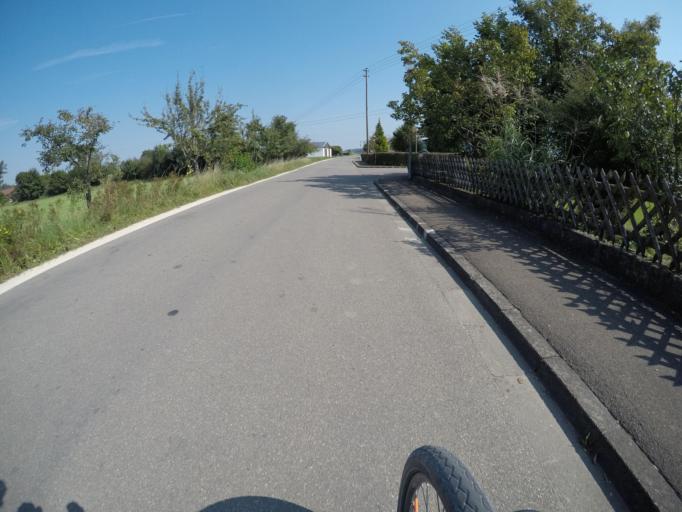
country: DE
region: Bavaria
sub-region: Swabia
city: Holzheim
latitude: 48.5236
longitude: 10.5596
